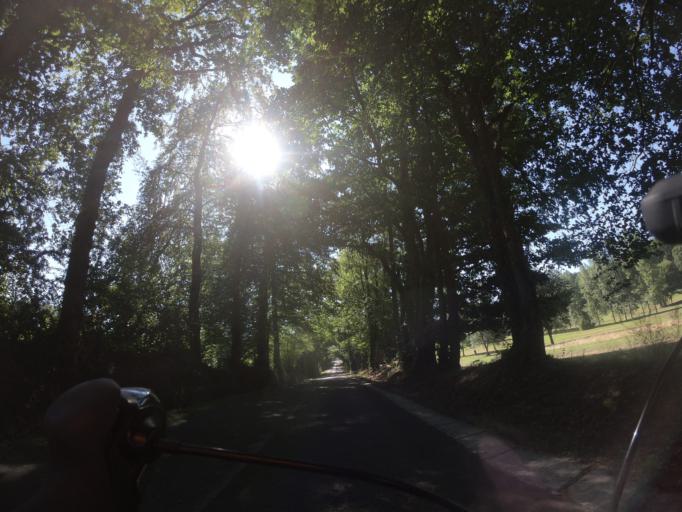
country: FR
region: Lower Normandy
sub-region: Departement de l'Orne
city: Tesse-la-Madeleine
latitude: 48.5660
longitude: -0.4377
